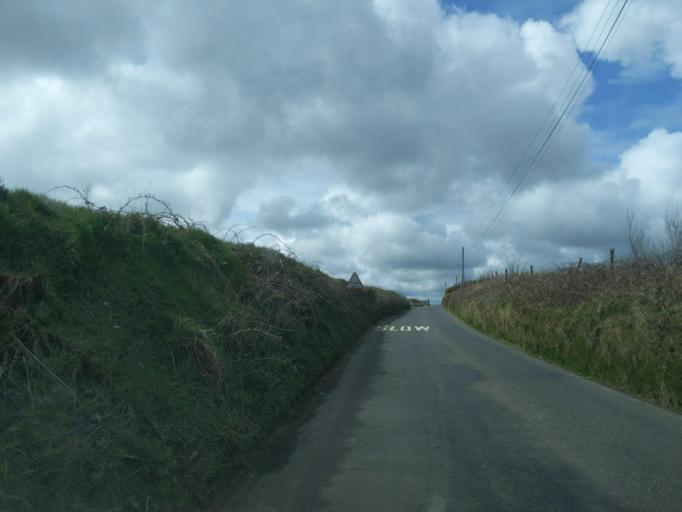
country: GB
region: England
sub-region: Cornwall
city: Camelford
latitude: 50.6271
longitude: -4.5959
